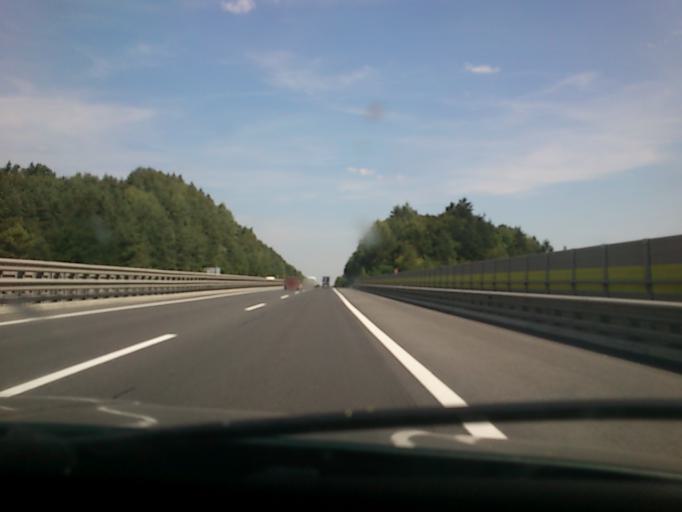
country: AT
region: Lower Austria
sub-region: Politischer Bezirk Neunkirchen
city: Warth
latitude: 47.6530
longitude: 16.1239
